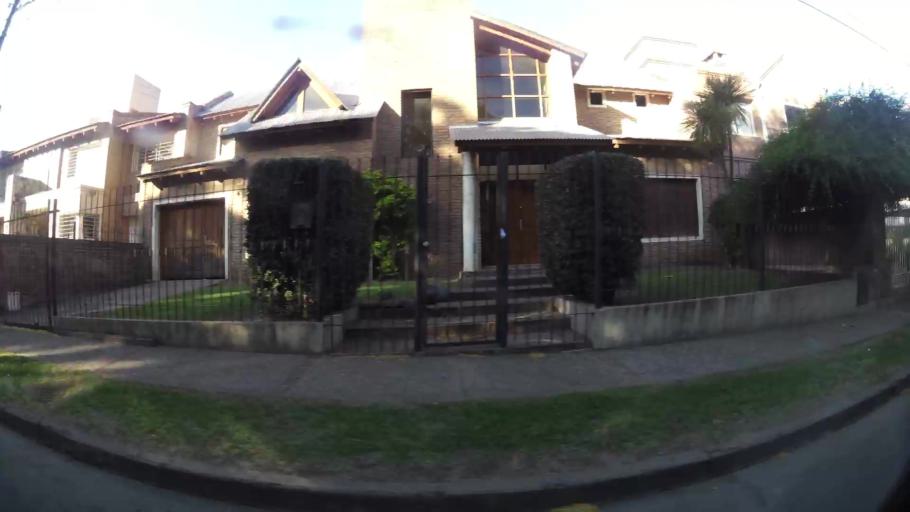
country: AR
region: Cordoba
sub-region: Departamento de Capital
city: Cordoba
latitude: -31.3879
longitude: -64.2389
